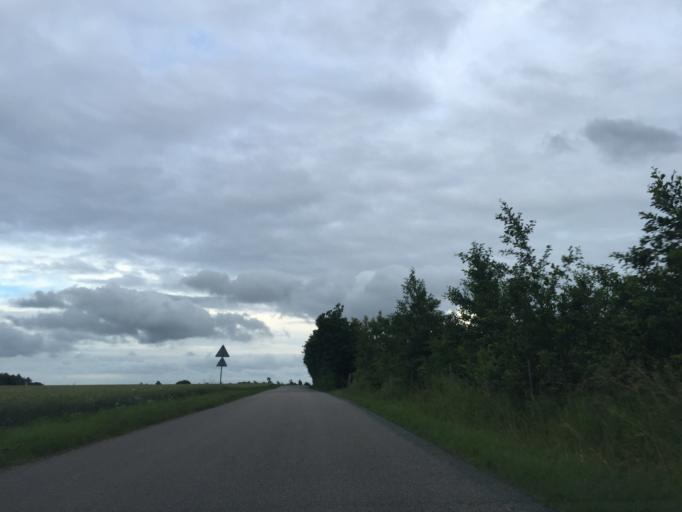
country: DK
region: Central Jutland
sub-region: Silkeborg Kommune
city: Silkeborg
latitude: 56.2430
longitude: 9.5355
